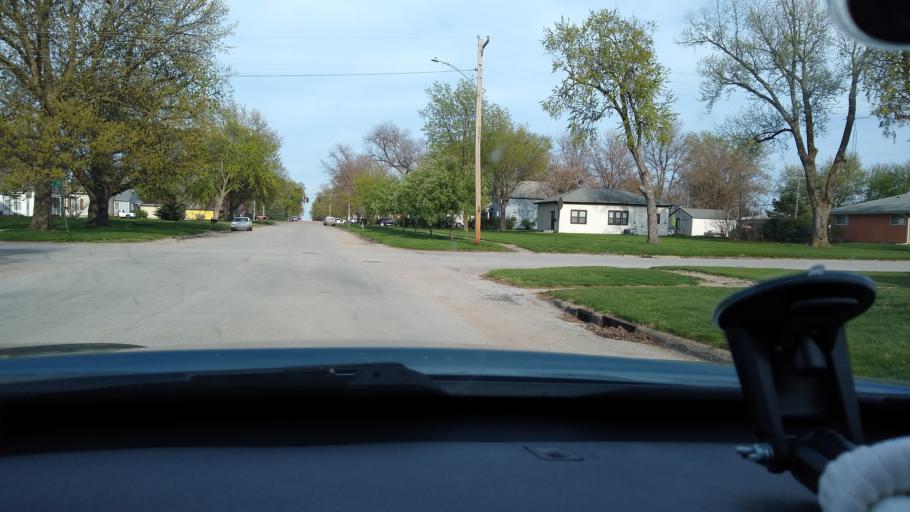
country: US
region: Nebraska
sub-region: Fillmore County
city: Geneva
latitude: 40.5270
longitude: -97.5979
